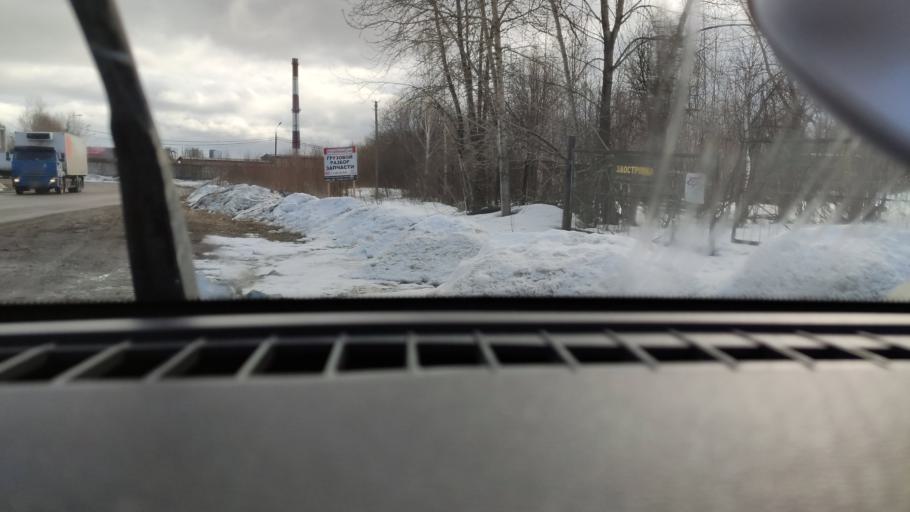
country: RU
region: Perm
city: Kondratovo
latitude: 57.9990
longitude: 56.1058
